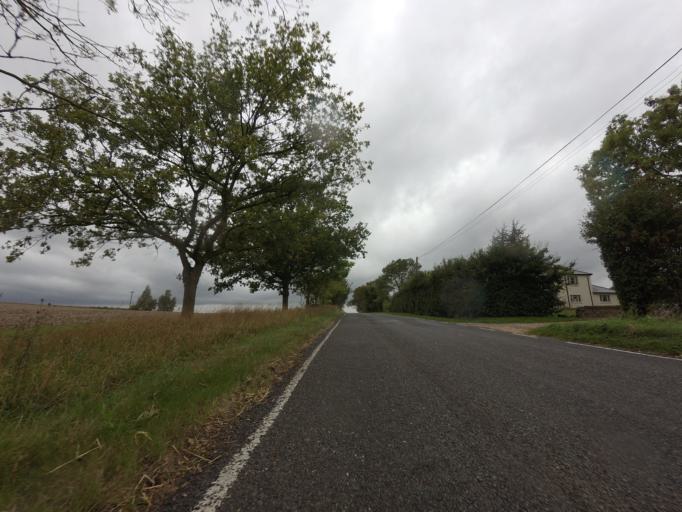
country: GB
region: England
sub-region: Cambridgeshire
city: Comberton
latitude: 52.1711
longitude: -0.0161
